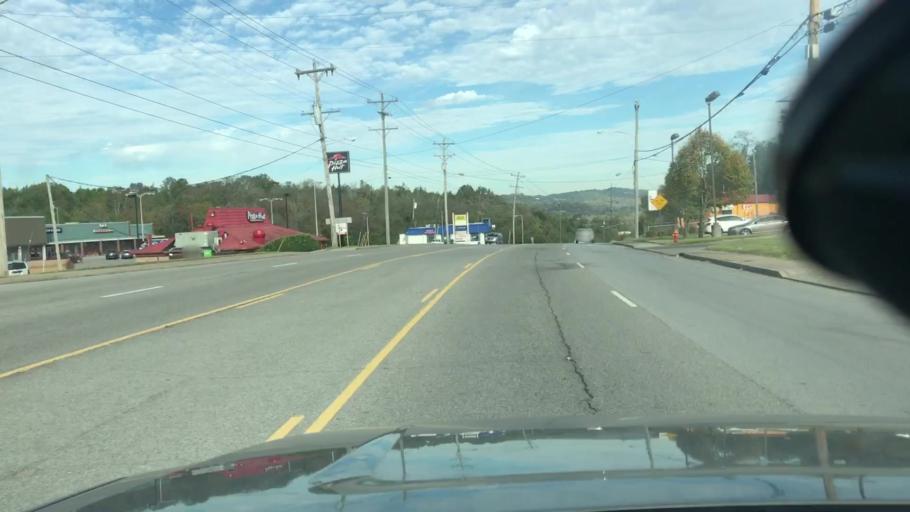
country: US
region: Tennessee
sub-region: Davidson County
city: Nashville
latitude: 36.1982
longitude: -86.8378
